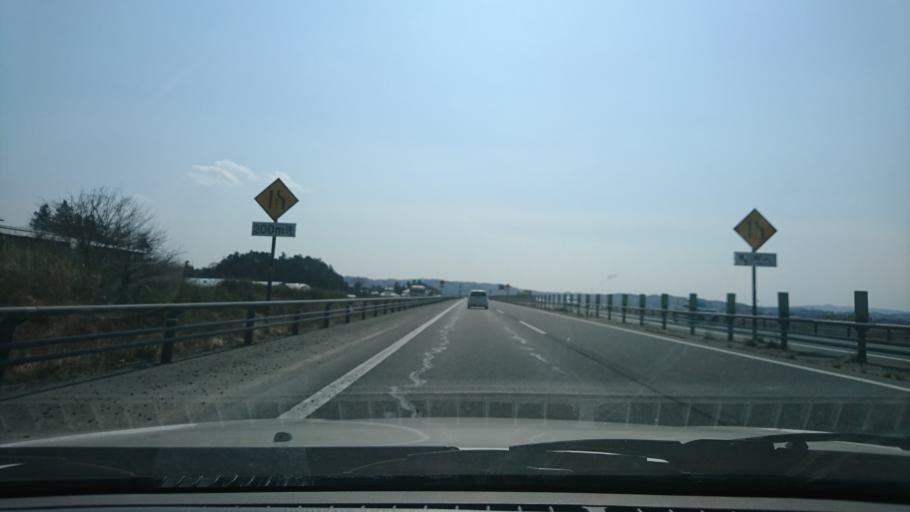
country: JP
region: Miyagi
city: Wakuya
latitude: 38.6716
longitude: 141.2657
